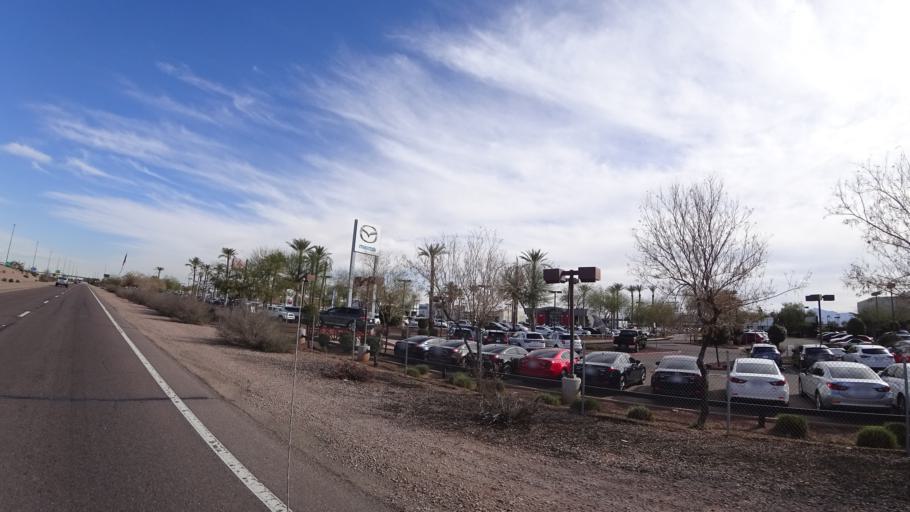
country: US
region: Arizona
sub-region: Maricopa County
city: Tolleson
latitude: 33.4607
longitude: -112.2887
